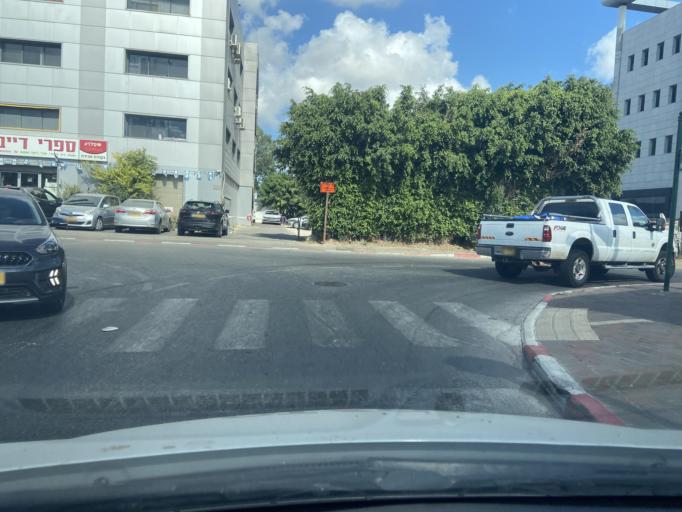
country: IL
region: Central District
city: Yehud
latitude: 32.0273
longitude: 34.8939
